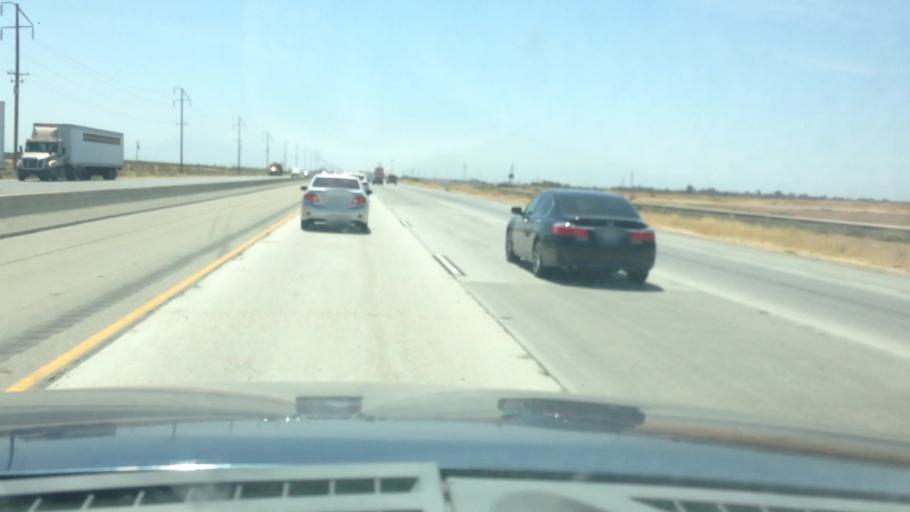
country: US
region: California
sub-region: Kern County
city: Greenacres
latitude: 35.4653
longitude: -119.1191
